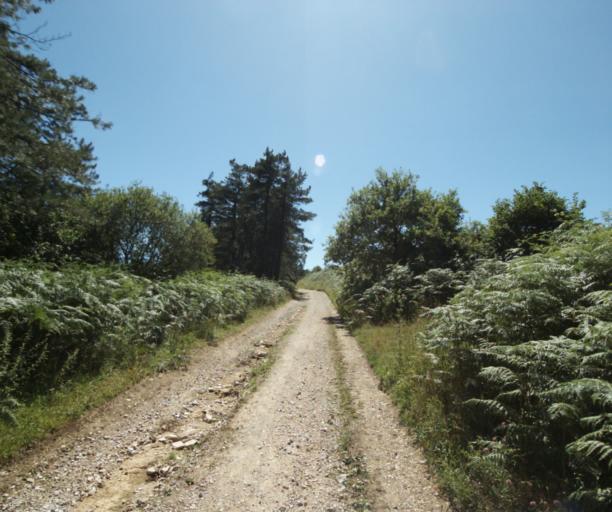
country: FR
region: Midi-Pyrenees
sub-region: Departement du Tarn
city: Dourgne
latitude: 43.4514
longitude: 2.1580
